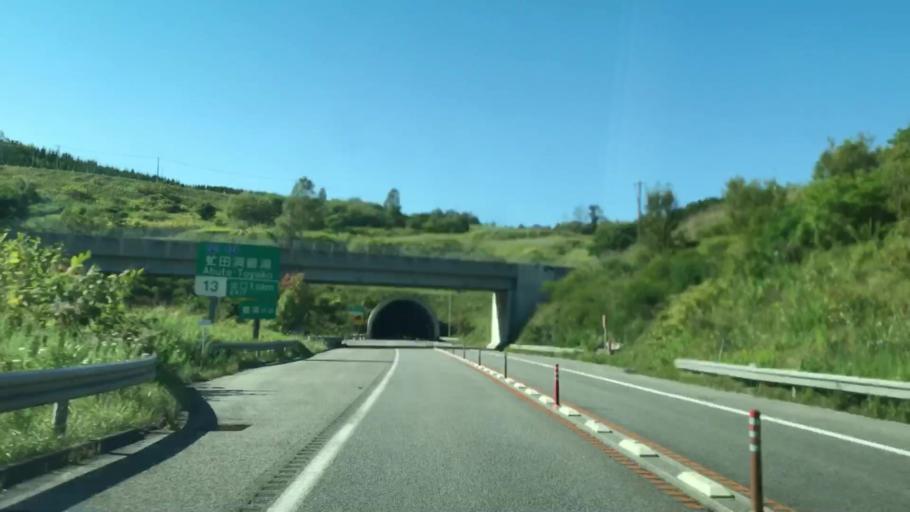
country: JP
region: Hokkaido
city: Date
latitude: 42.5514
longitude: 140.7892
